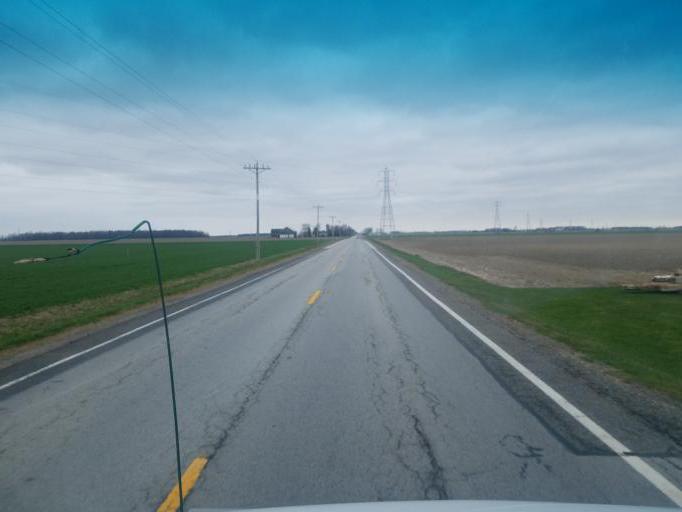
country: US
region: Ohio
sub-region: Allen County
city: Delphos
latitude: 40.9324
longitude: -84.3815
